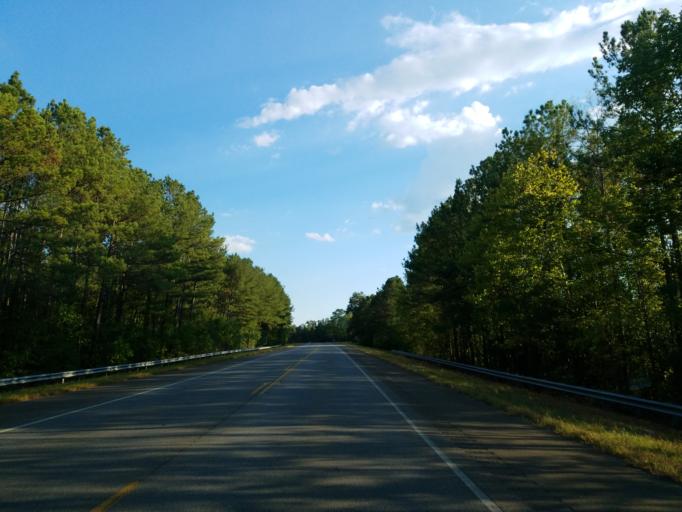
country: US
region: Georgia
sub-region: Murray County
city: Chatsworth
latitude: 34.6569
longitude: -84.7201
